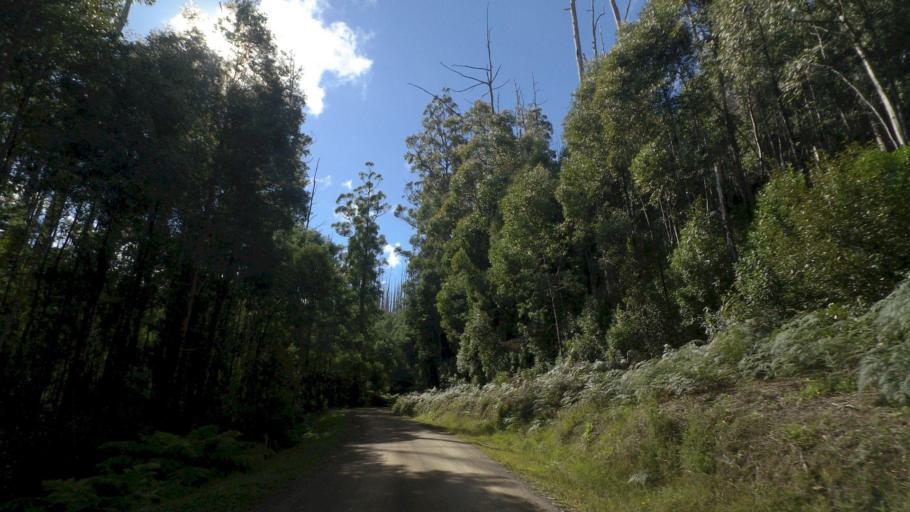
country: AU
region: Victoria
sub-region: Cardinia
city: Bunyip
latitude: -37.9533
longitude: 145.8196
